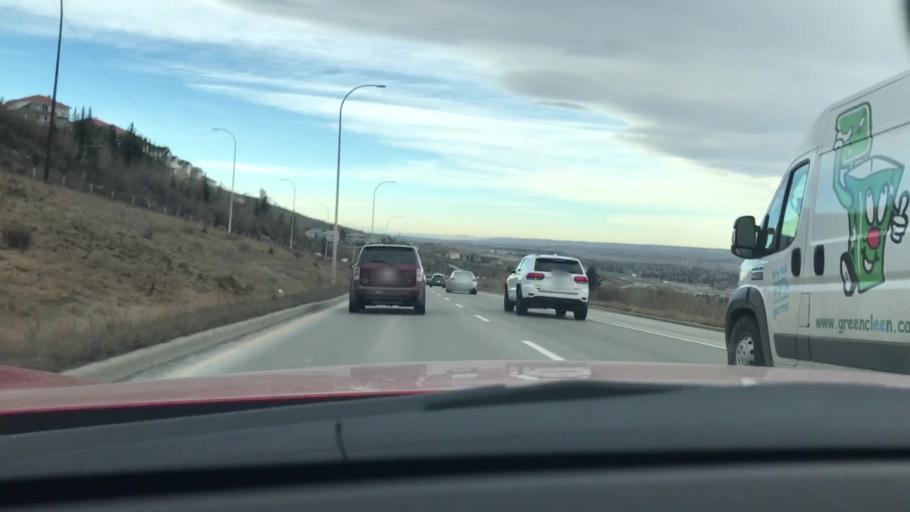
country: CA
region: Alberta
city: Calgary
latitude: 51.0668
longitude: -114.1729
